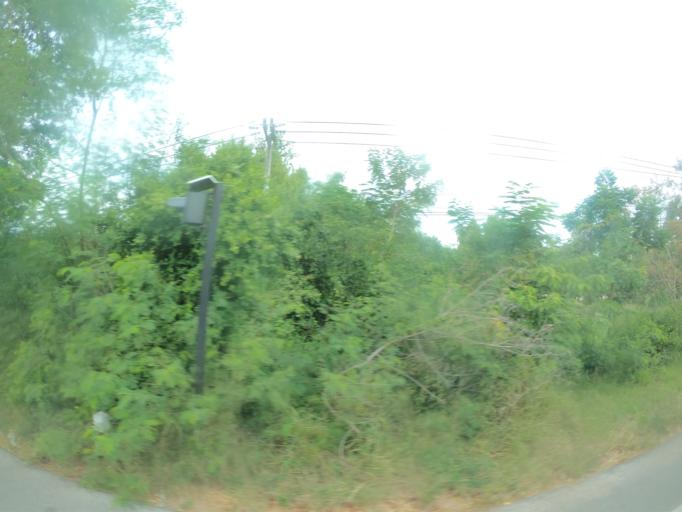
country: TH
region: Maha Sarakham
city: Kantharawichai
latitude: 16.3373
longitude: 103.2253
